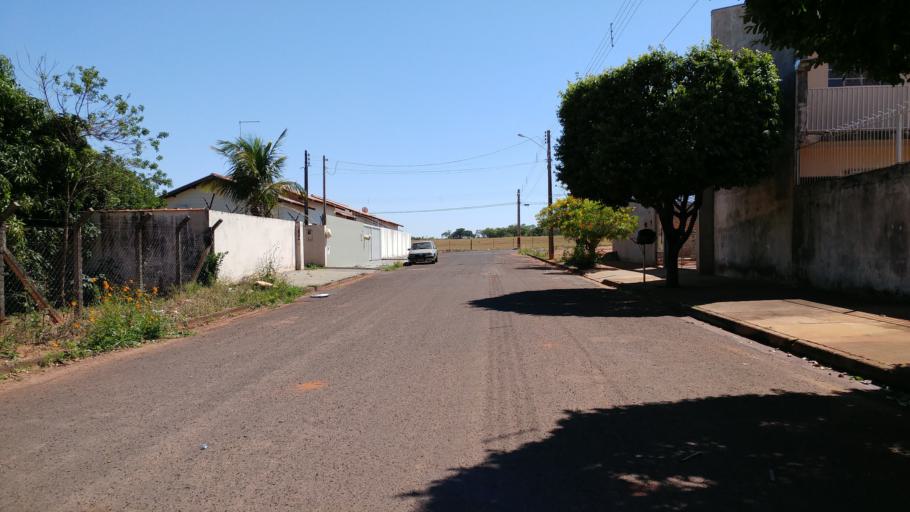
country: BR
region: Sao Paulo
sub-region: Paraguacu Paulista
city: Paraguacu Paulista
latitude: -22.4096
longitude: -50.5901
